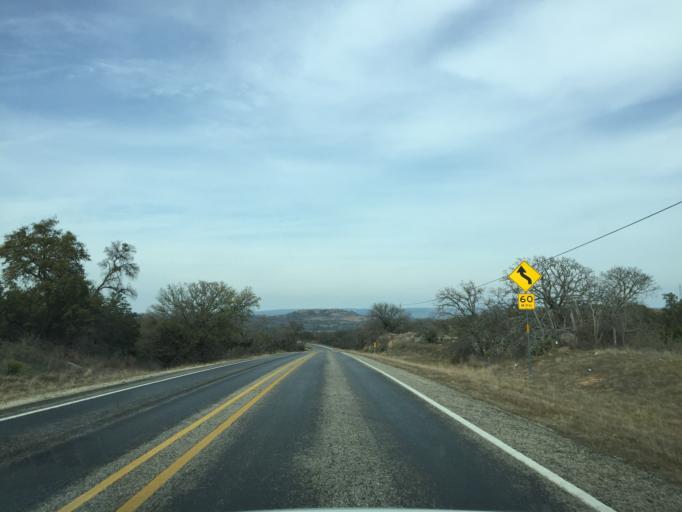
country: US
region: Texas
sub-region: Gillespie County
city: Fredericksburg
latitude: 30.4519
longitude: -98.7315
